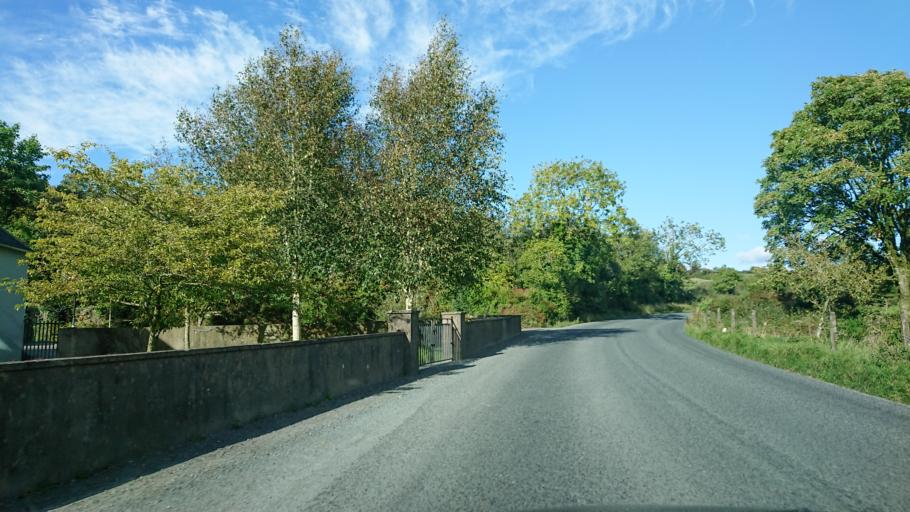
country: IE
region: Munster
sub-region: Waterford
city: Dungarvan
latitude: 52.1557
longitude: -7.6974
